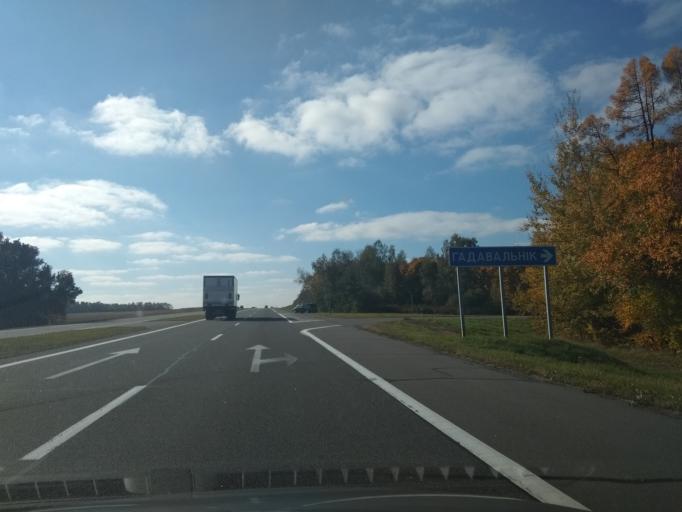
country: BY
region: Brest
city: Baranovichi
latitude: 53.2027
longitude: 26.0988
